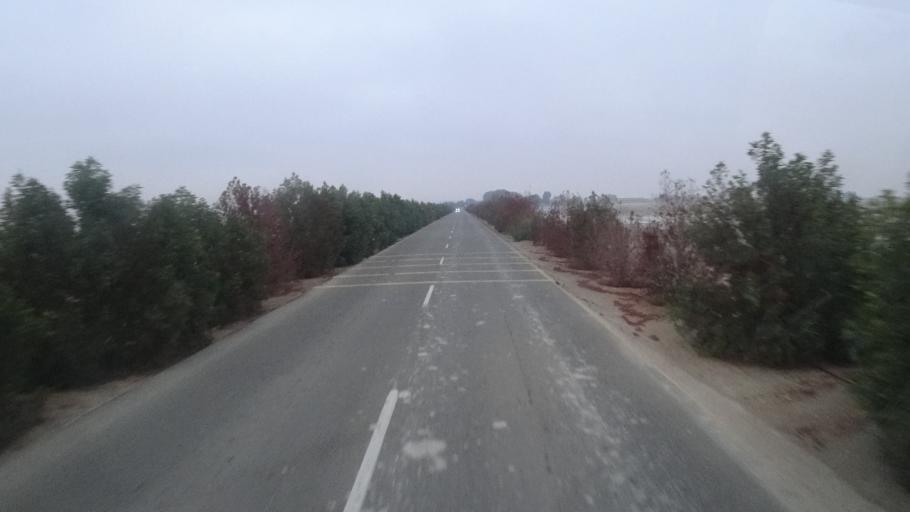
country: AE
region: Abu Dhabi
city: Abu Dhabi
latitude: 24.1928
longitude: 54.6997
